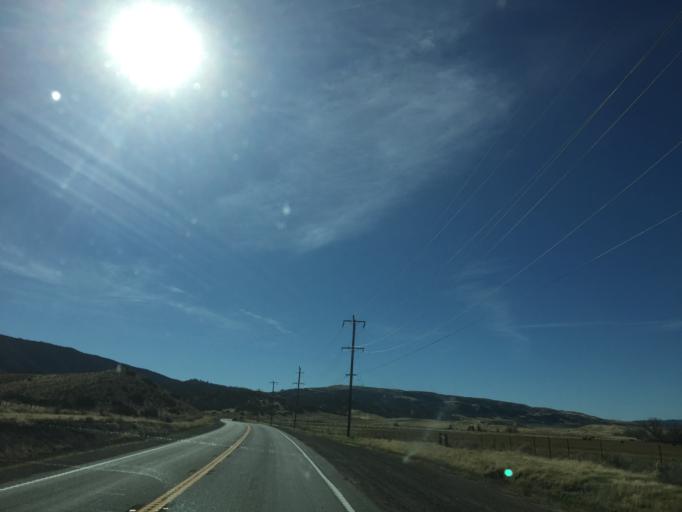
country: US
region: California
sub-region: Kern County
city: Lebec
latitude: 34.7796
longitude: -118.6711
